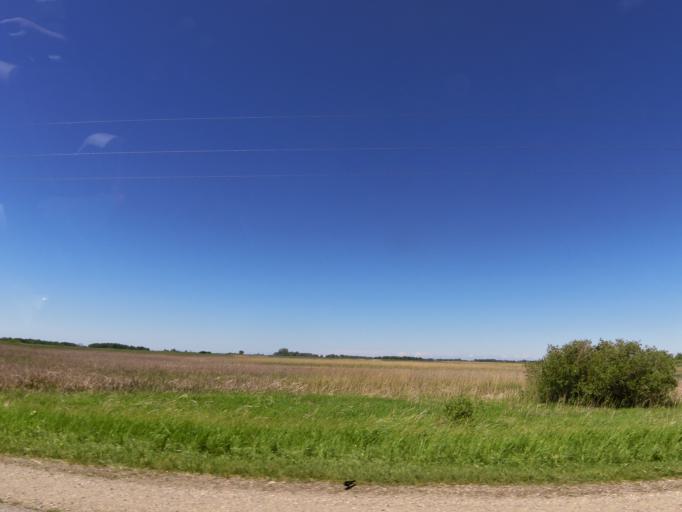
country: US
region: Minnesota
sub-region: Mahnomen County
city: Mahnomen
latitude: 47.2040
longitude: -95.9333
